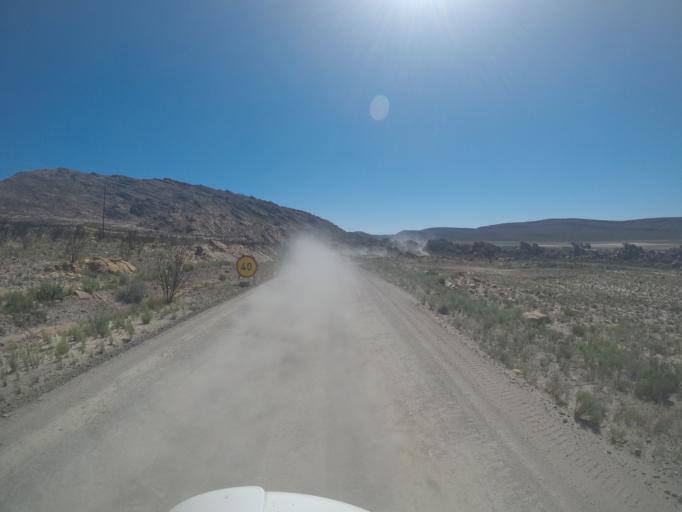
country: ZA
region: Western Cape
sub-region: Cape Winelands District Municipality
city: Ceres
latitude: -32.8495
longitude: 19.4456
